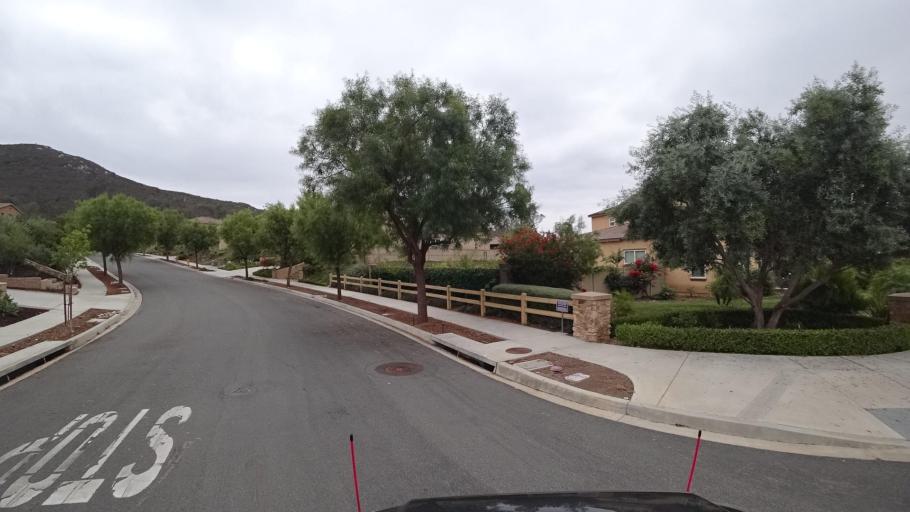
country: US
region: California
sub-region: San Diego County
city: Escondido
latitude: 33.0379
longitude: -117.1096
